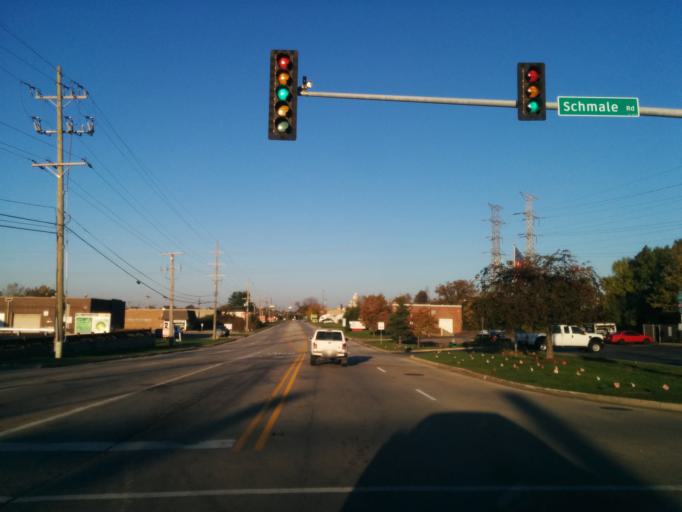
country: US
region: Illinois
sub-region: DuPage County
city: Wheaton
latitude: 41.8975
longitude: -88.1020
